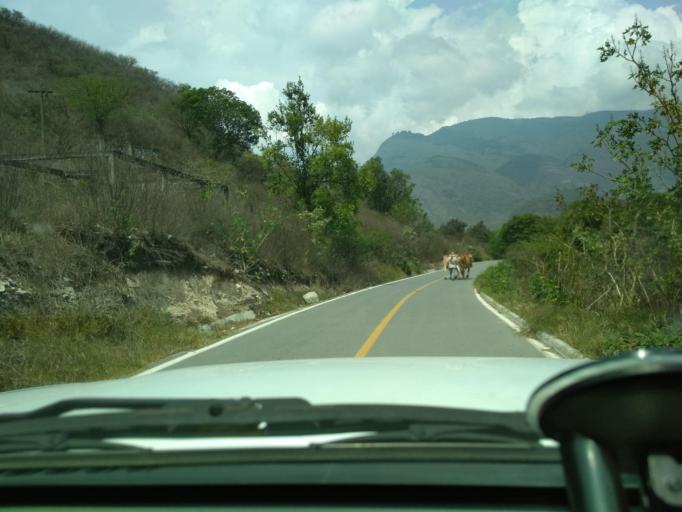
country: MX
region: Veracruz
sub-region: Nogales
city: Taza de Agua Ojo Zarco
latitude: 18.7829
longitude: -97.2135
